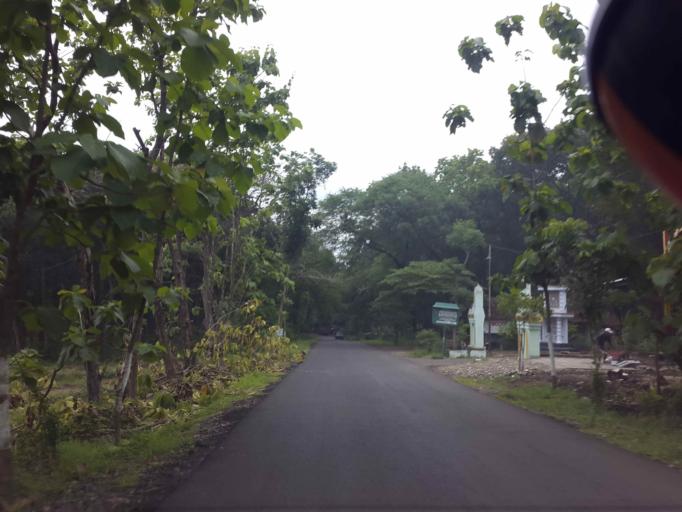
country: ID
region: East Java
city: Ponorogo
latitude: -7.7707
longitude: 111.3503
